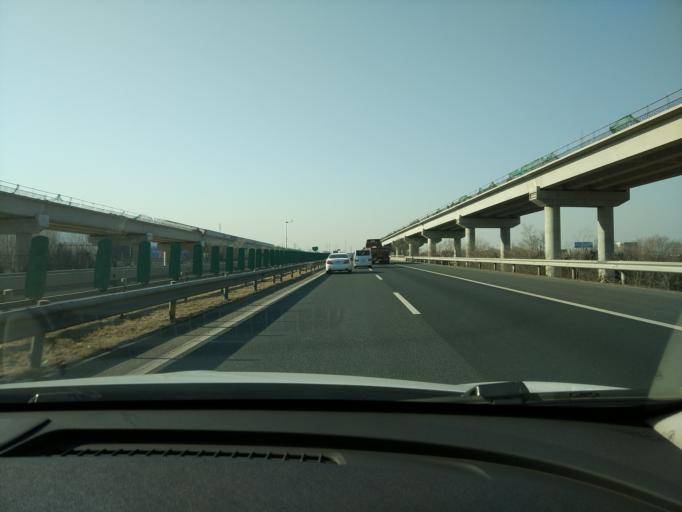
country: CN
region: Beijing
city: Kangzhuang
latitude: 40.3617
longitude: 115.9354
